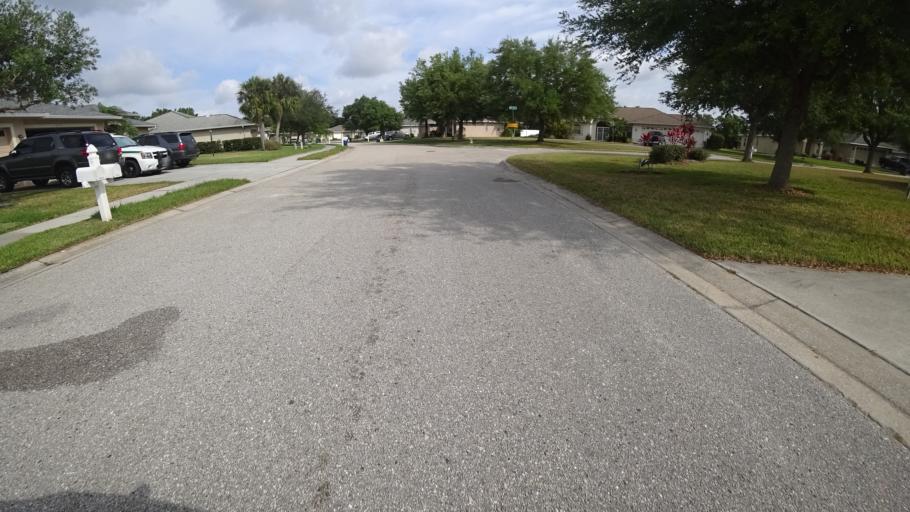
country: US
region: Florida
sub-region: Manatee County
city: Ellenton
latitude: 27.5714
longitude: -82.4717
